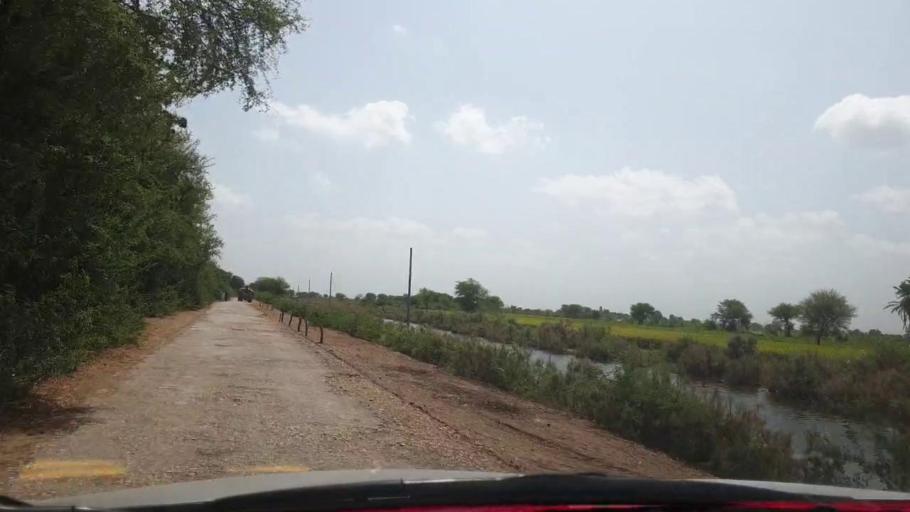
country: PK
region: Sindh
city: Talhar
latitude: 24.8943
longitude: 68.9060
